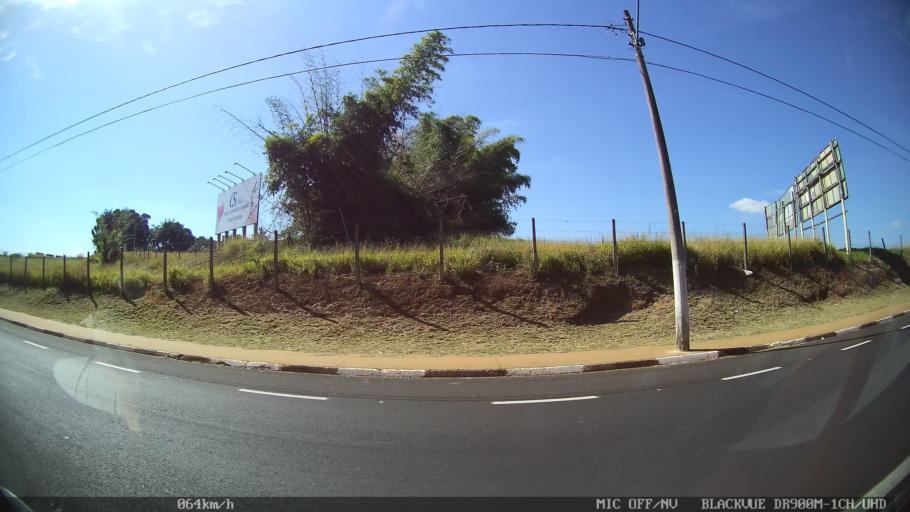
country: BR
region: Sao Paulo
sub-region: Franca
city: Franca
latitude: -20.5456
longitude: -47.4198
